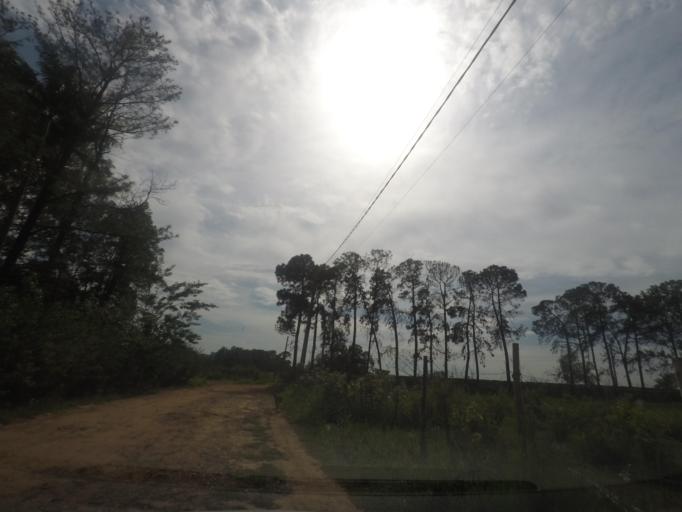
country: BR
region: Sao Paulo
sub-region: Sumare
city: Sumare
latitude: -22.7980
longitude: -47.2468
